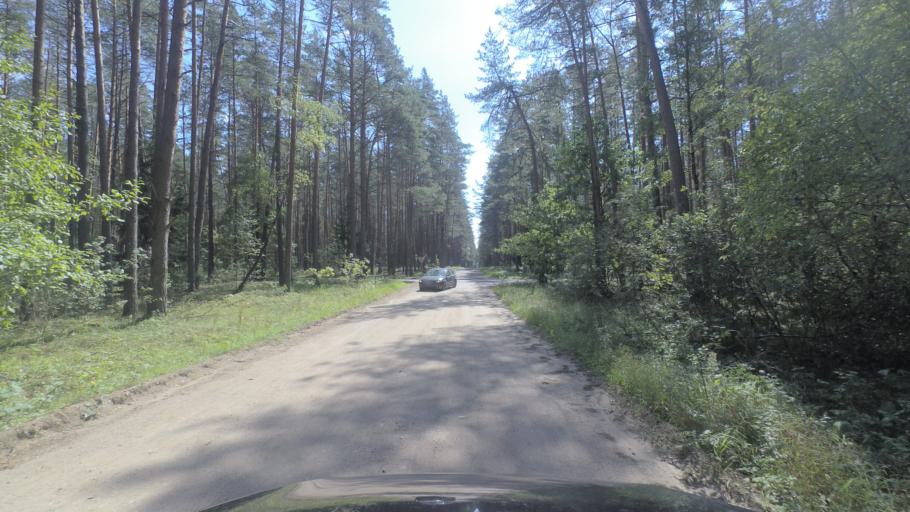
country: LT
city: Nemencine
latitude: 54.8452
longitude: 25.4981
